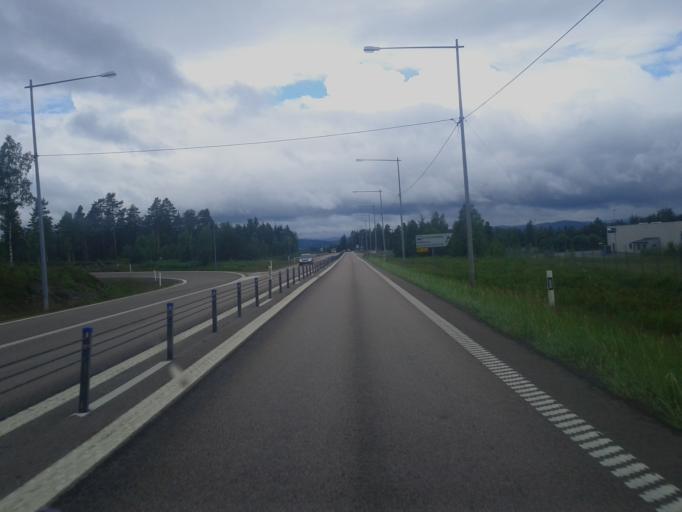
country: SE
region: Vaesternorrland
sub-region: Haernoesands Kommun
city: Haernoesand
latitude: 62.6523
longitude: 17.8873
